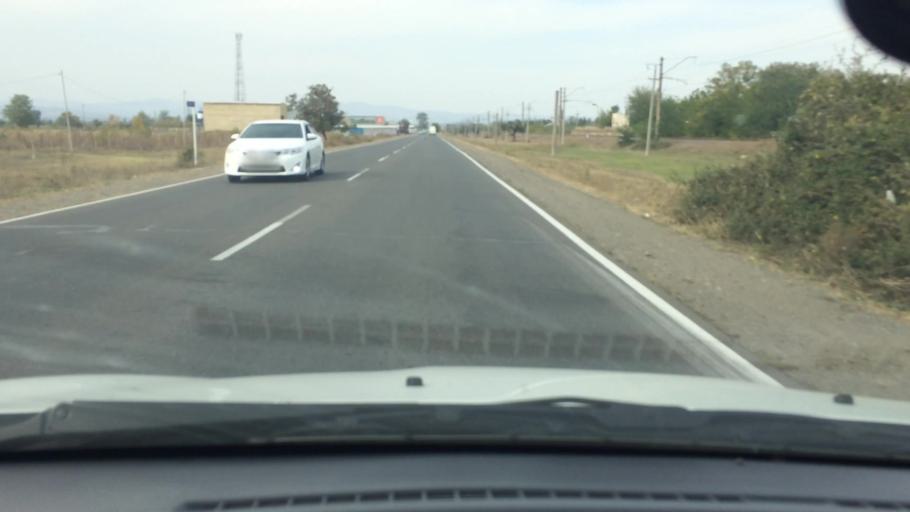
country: GE
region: Kvemo Kartli
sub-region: Marneuli
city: Marneuli
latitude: 41.4333
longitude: 44.8202
